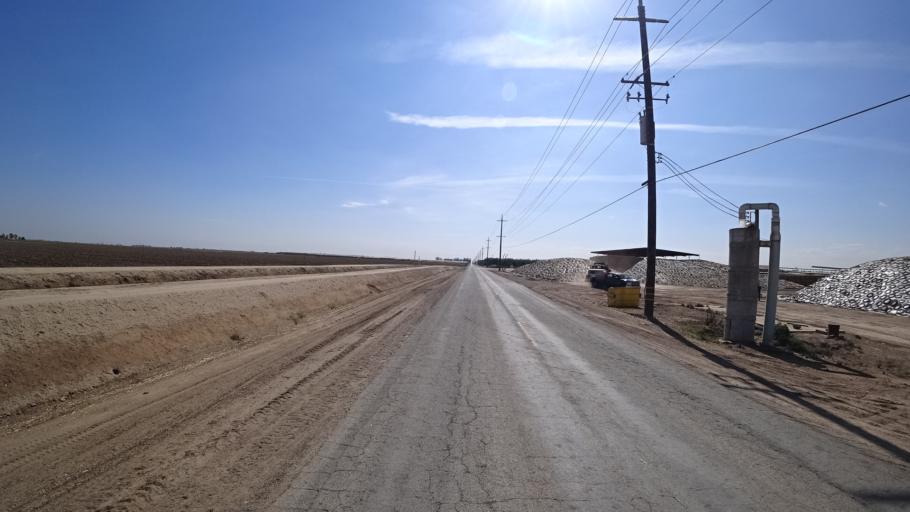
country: US
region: California
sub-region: Kings County
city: Home Garden
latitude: 36.2549
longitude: -119.6154
